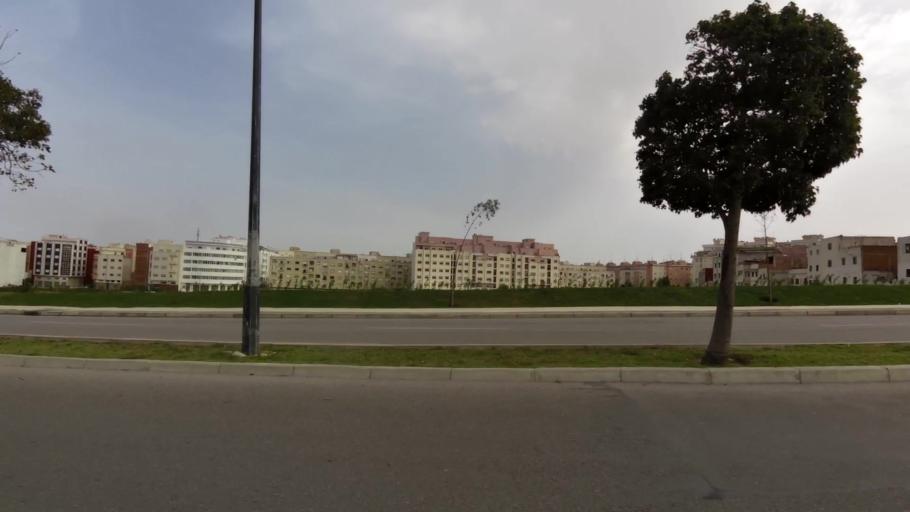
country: MA
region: Tanger-Tetouan
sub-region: Tanger-Assilah
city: Boukhalef
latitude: 35.7478
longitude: -5.8494
